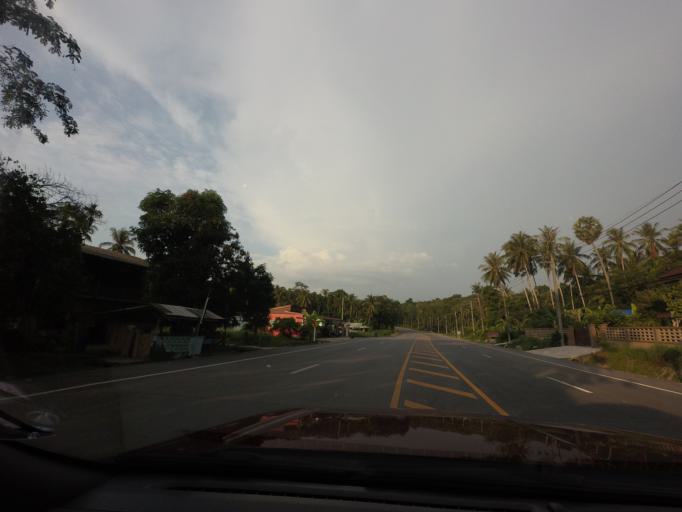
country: TH
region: Pattani
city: Khok Pho
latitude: 6.6745
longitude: 101.1133
